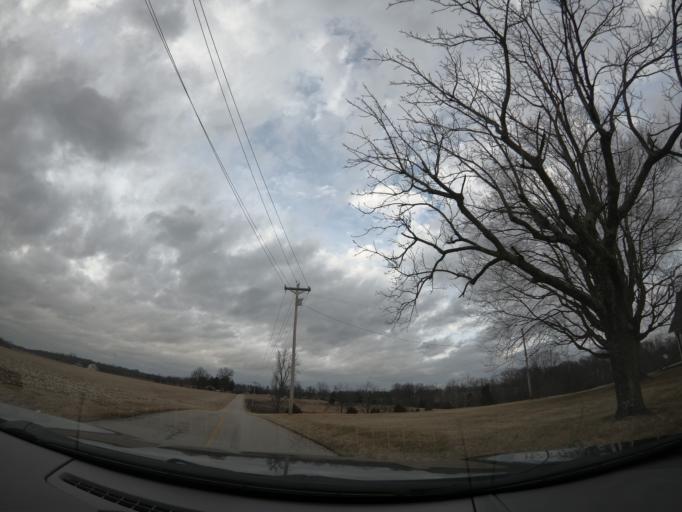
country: US
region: Indiana
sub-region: Floyd County
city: Galena
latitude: 38.3787
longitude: -85.9107
